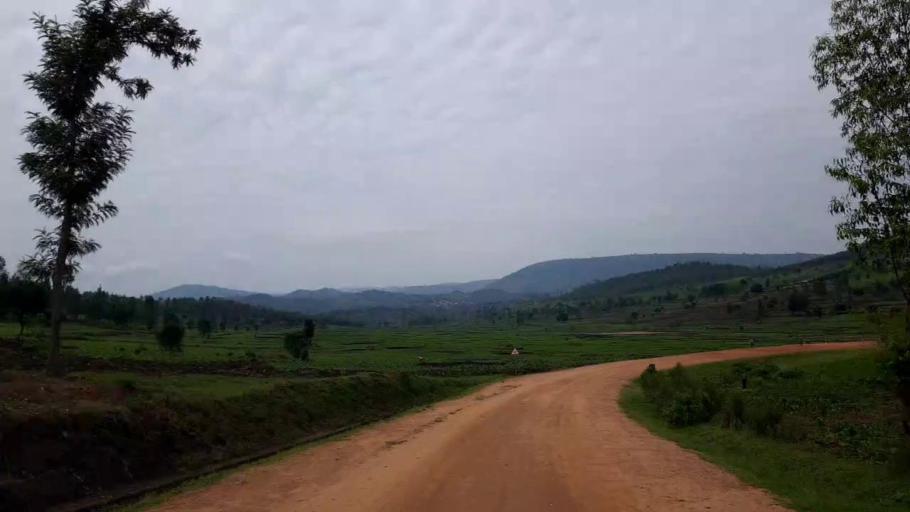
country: RW
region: Northern Province
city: Byumba
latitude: -1.5003
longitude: 30.2313
